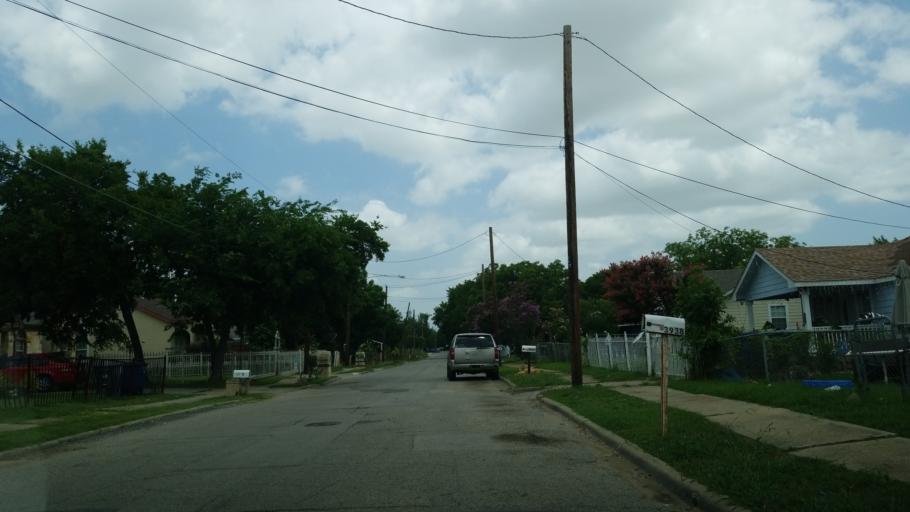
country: US
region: Texas
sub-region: Dallas County
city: Irving
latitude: 32.7900
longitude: -96.9024
